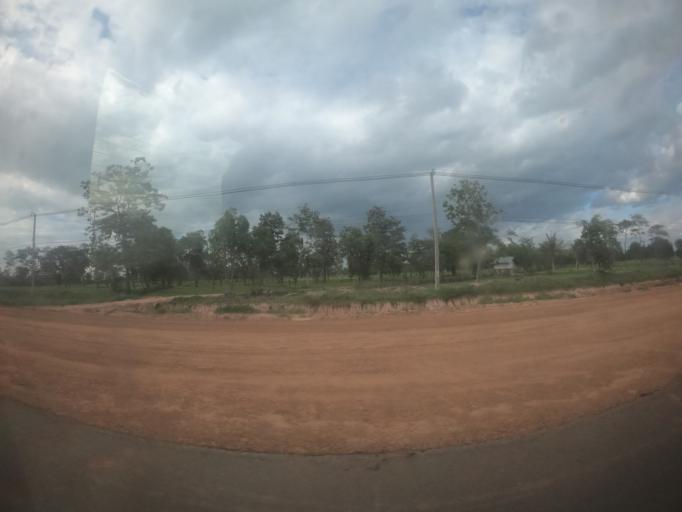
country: TH
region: Surin
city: Kap Choeng
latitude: 14.5124
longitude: 103.5506
